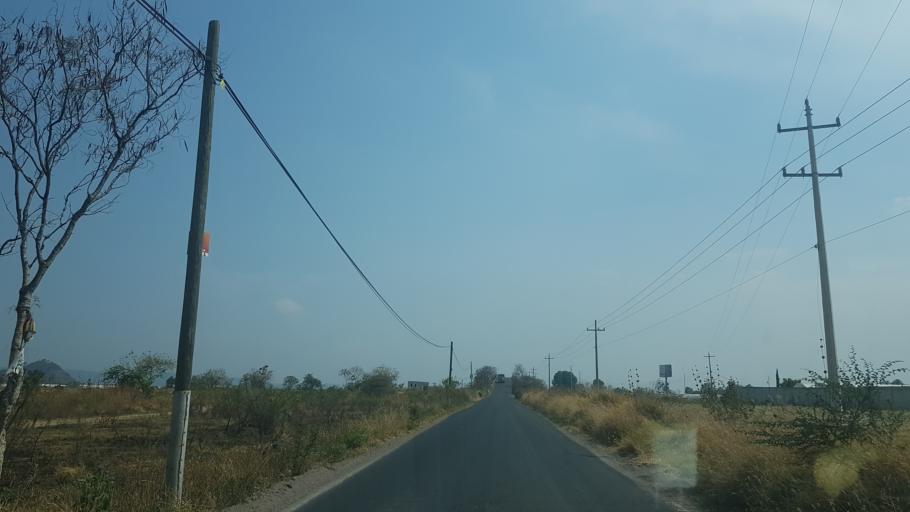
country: MX
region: Puebla
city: San Juan Tianguismanalco
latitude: 18.9381
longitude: -98.4541
